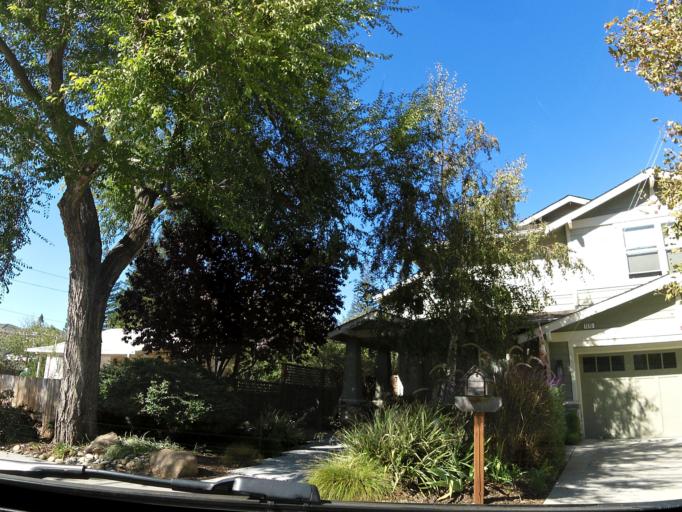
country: US
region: California
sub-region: Santa Clara County
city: Campbell
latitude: 37.2741
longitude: -121.9730
